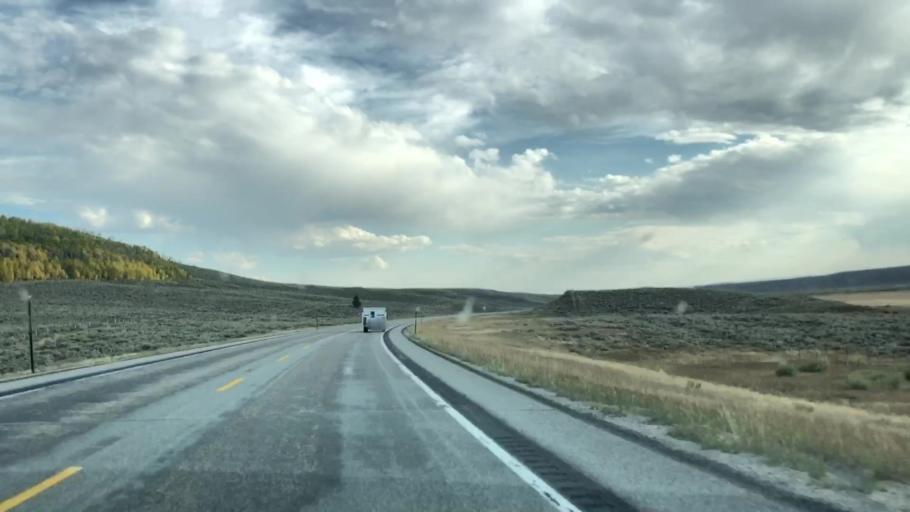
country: US
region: Wyoming
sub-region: Sublette County
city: Pinedale
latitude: 43.0858
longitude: -110.1629
